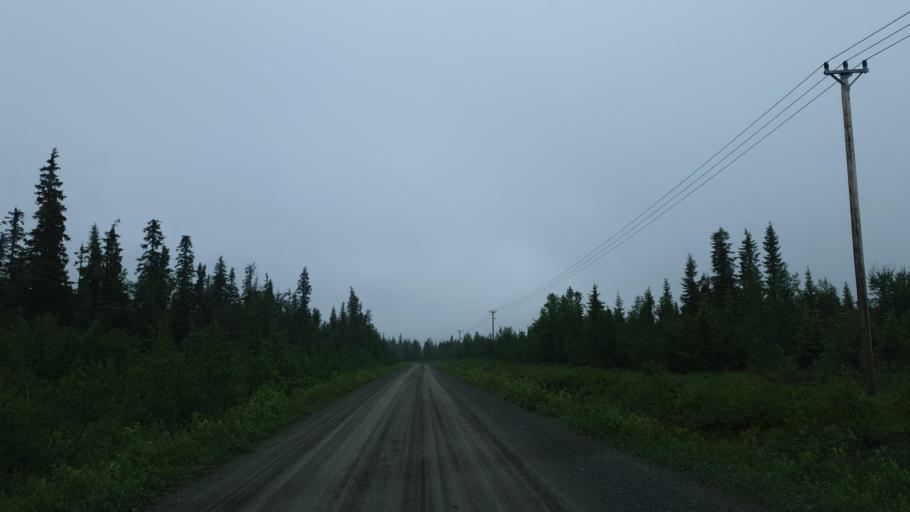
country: SE
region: Vaesterbotten
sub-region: Vilhelmina Kommun
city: Sjoberg
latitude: 65.3126
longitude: 15.9655
